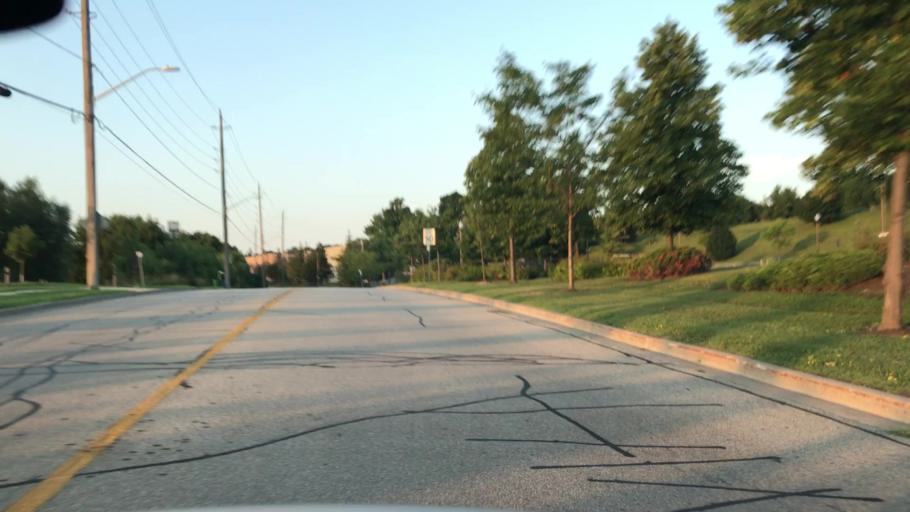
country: CA
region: Ontario
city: Newmarket
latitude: 44.0177
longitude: -79.4623
